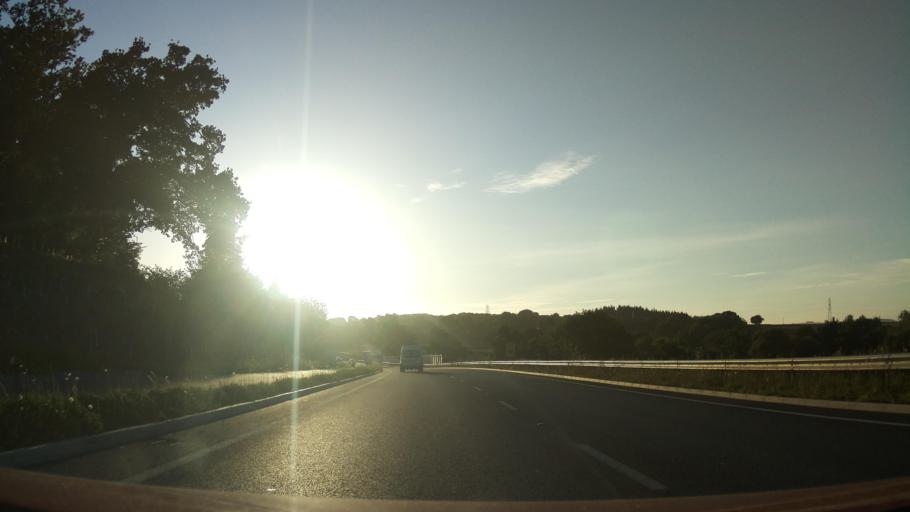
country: GB
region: England
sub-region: Devon
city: Newton Abbot
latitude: 50.5430
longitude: -3.6209
